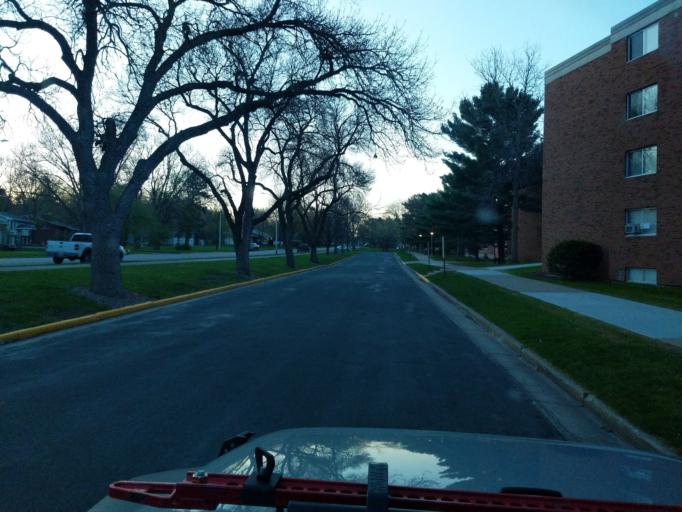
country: US
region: Wisconsin
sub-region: Pierce County
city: River Falls
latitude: 44.8533
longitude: -92.6168
